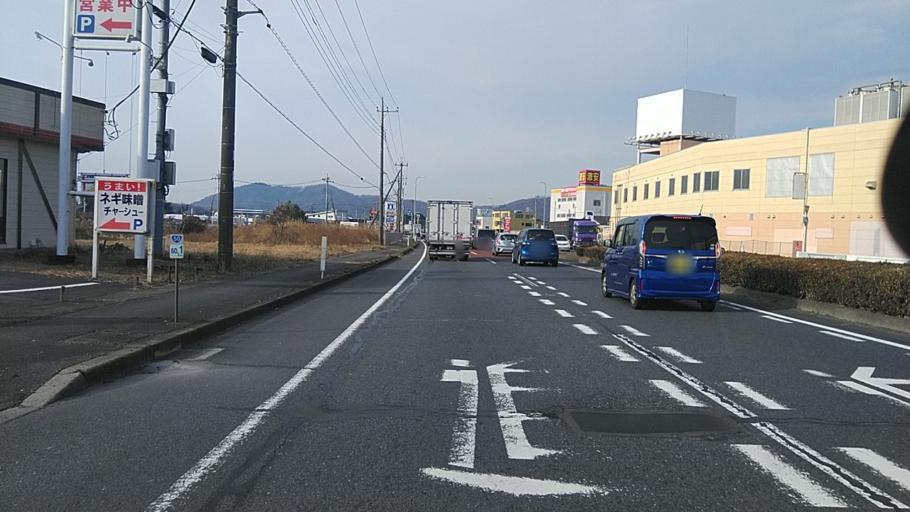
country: JP
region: Tochigi
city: Fujioka
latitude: 36.3144
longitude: 139.6613
